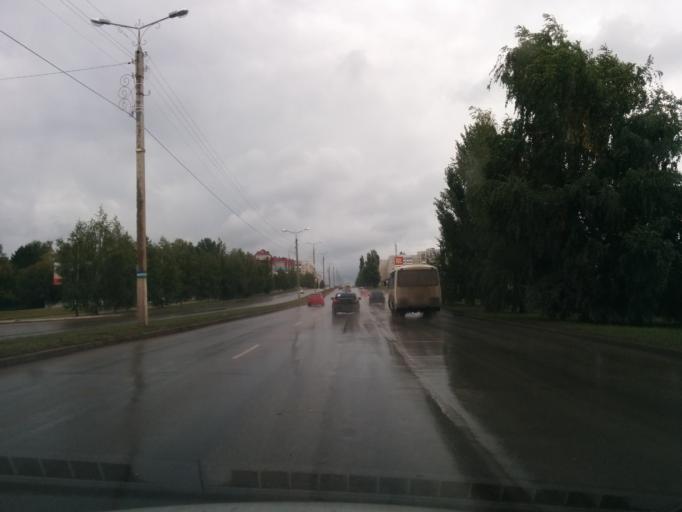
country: RU
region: Bashkortostan
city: Oktyabr'skiy
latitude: 54.4827
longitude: 53.5055
